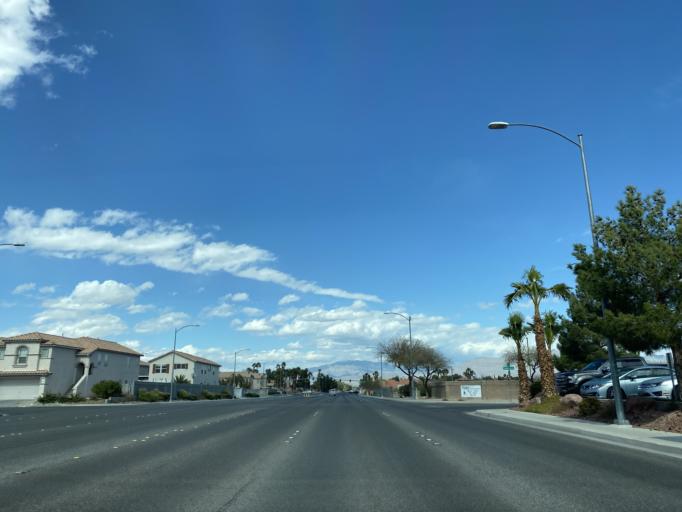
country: US
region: Nevada
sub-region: Clark County
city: Spring Valley
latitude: 36.2307
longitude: -115.2606
